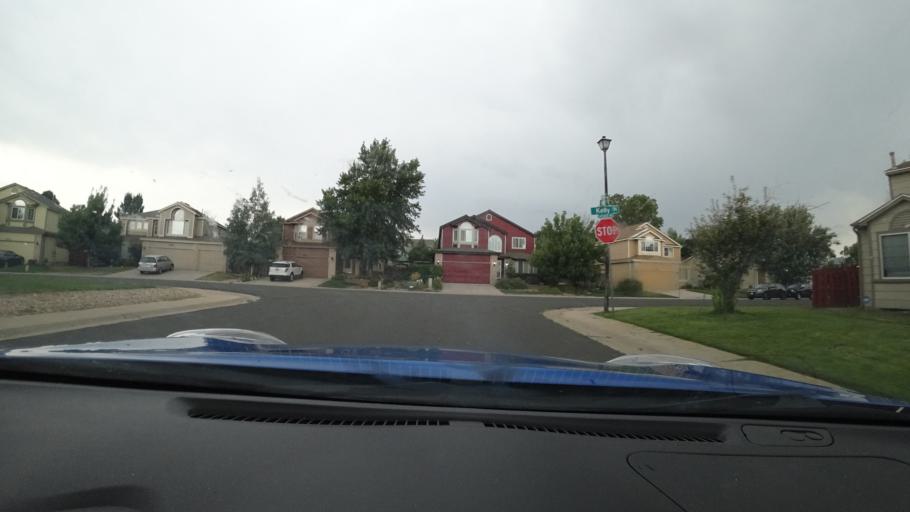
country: US
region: Colorado
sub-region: Adams County
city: Aurora
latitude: 39.7763
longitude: -104.7496
